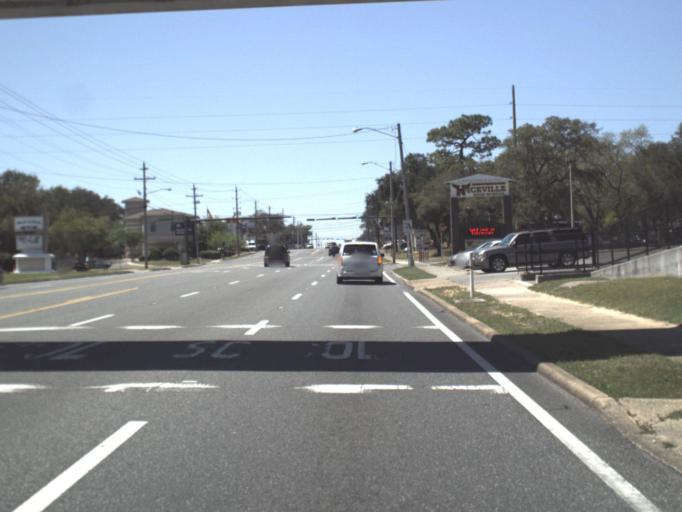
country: US
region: Florida
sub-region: Okaloosa County
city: Niceville
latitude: 30.5184
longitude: -86.4765
